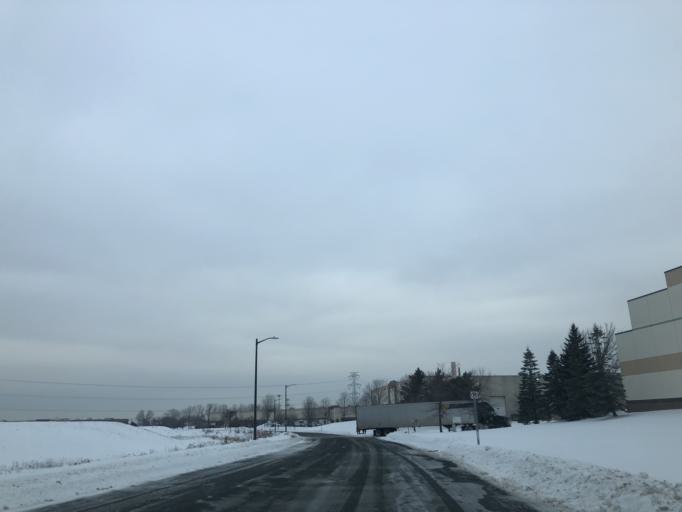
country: US
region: Minnesota
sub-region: Ramsey County
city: New Brighton
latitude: 45.0691
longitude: -93.1800
